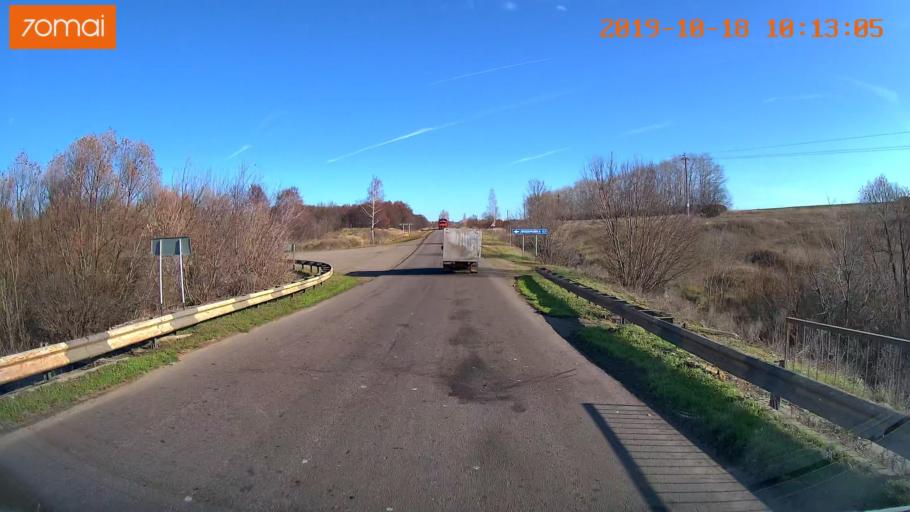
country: RU
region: Tula
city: Kurkino
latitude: 53.3988
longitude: 38.5168
